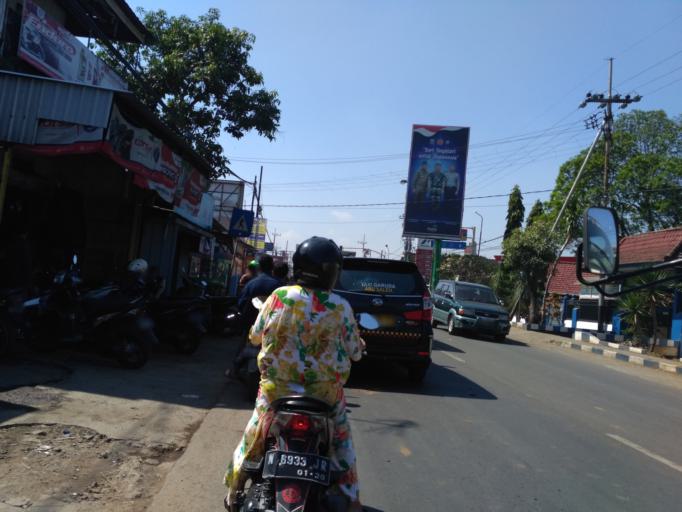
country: ID
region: East Java
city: Tamiajeng
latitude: -7.9525
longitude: 112.6893
